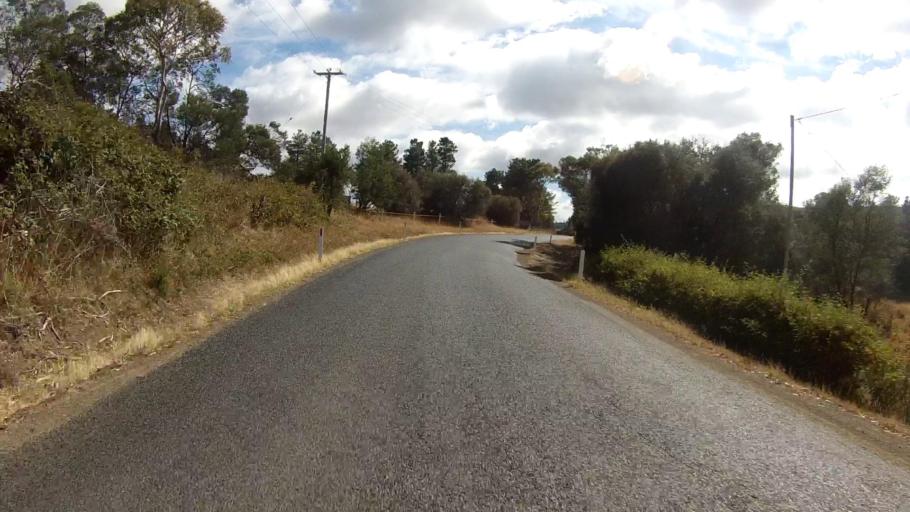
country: AU
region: Tasmania
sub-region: Brighton
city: Old Beach
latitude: -42.7730
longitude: 147.2881
